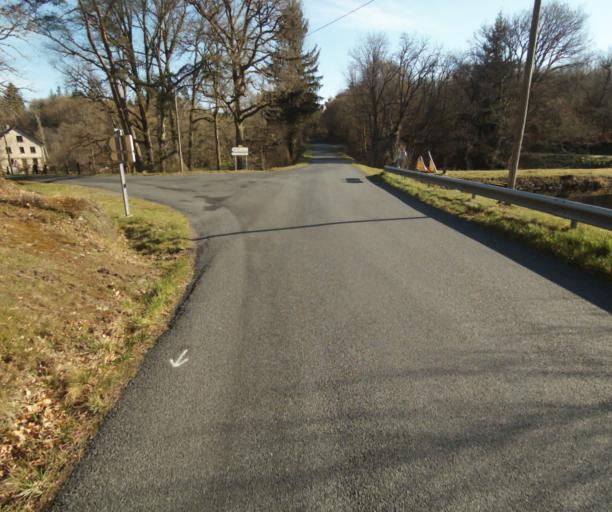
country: FR
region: Limousin
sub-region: Departement de la Correze
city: Correze
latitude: 45.3060
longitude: 1.8787
